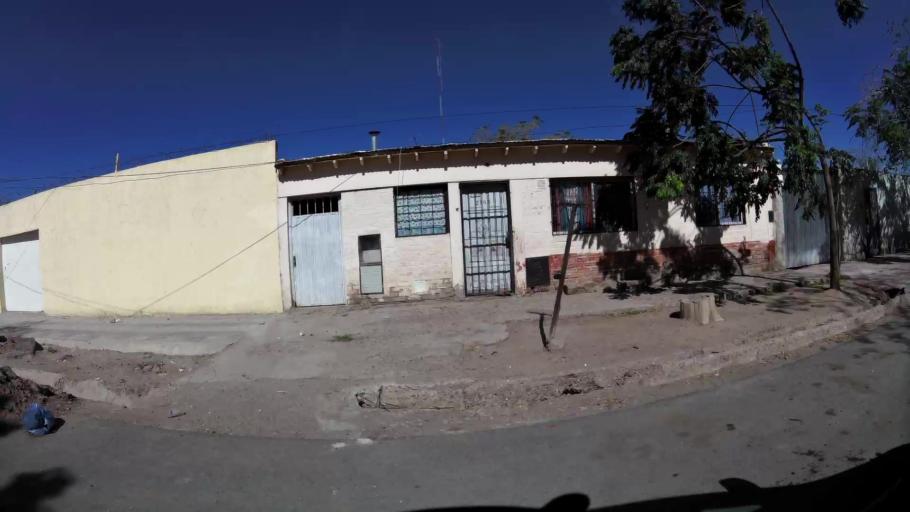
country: AR
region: Mendoza
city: Las Heras
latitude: -32.8377
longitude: -68.8159
